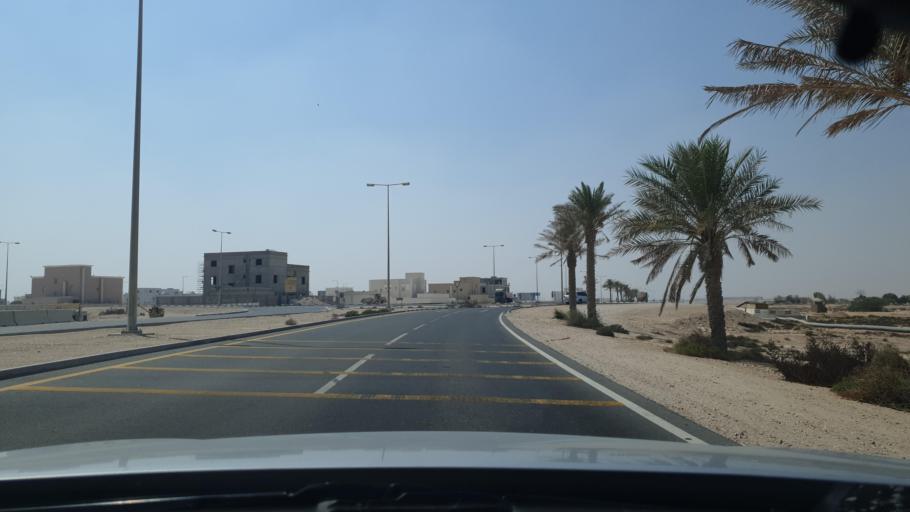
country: QA
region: Al Khawr
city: Al Khawr
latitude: 25.6777
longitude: 51.4765
